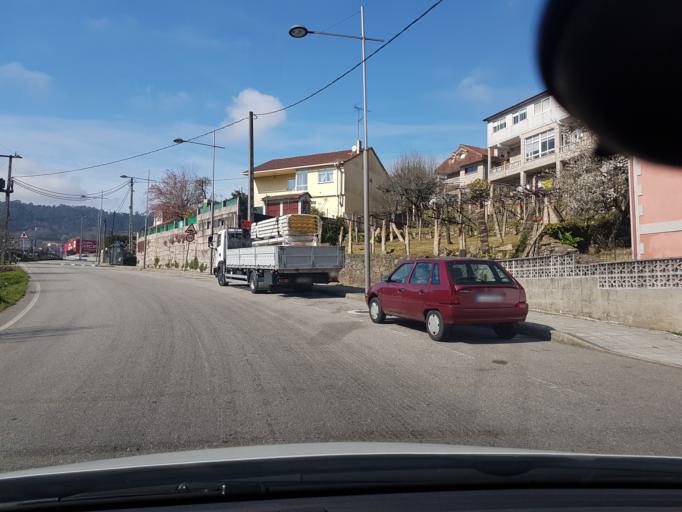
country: ES
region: Galicia
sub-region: Provincia de Pontevedra
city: Porrino
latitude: 42.1949
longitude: -8.6454
